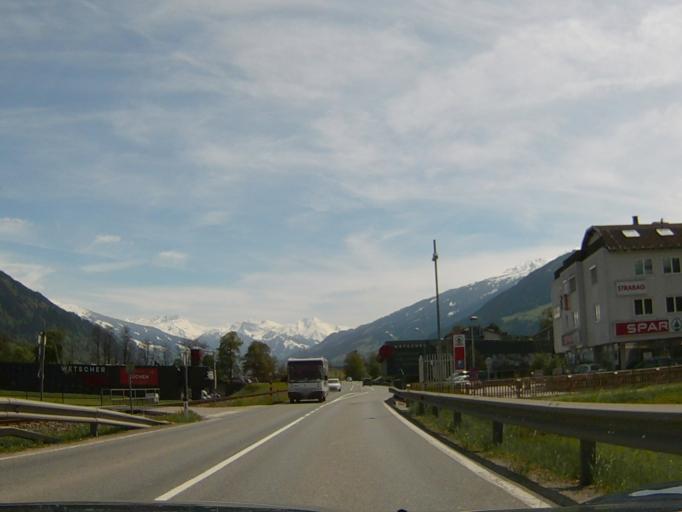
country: AT
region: Tyrol
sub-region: Politischer Bezirk Schwaz
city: Fugen
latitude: 47.3492
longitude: 11.8521
